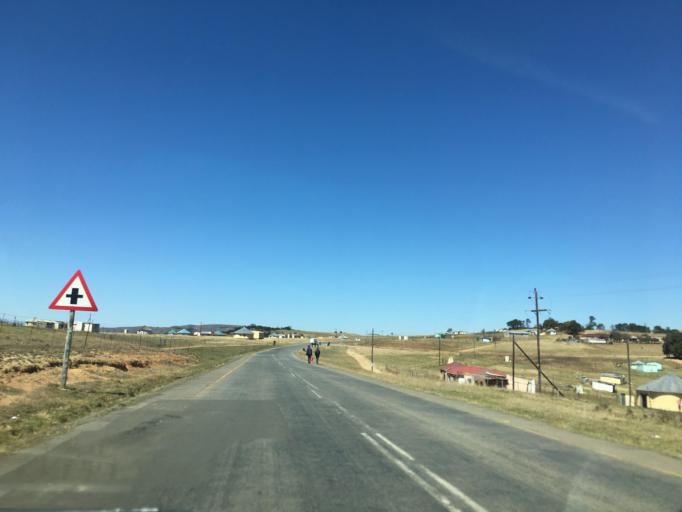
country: ZA
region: Eastern Cape
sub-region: Chris Hani District Municipality
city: Cala
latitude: -31.5553
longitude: 27.8955
